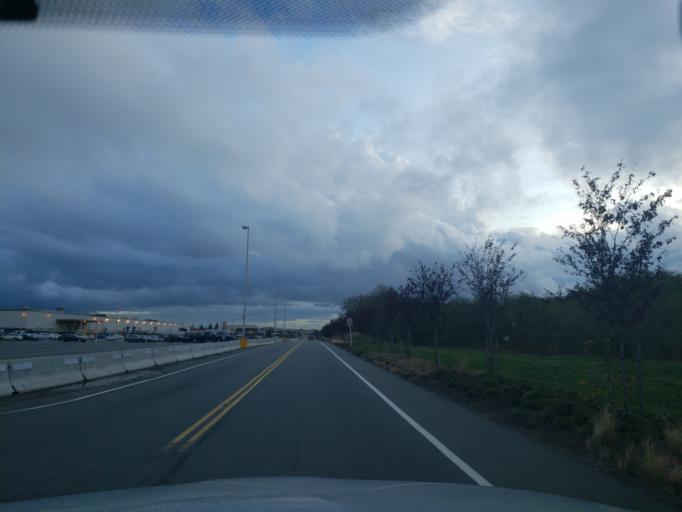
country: US
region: Washington
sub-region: Snohomish County
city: Mukilteo
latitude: 47.9326
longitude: -122.2848
